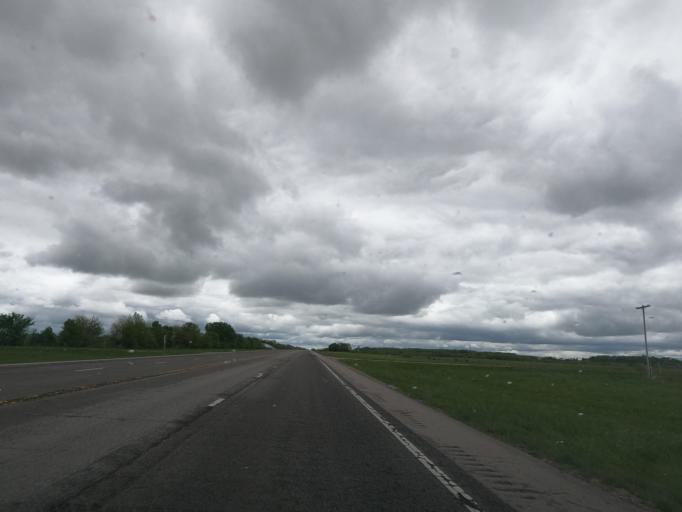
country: US
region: Kansas
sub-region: Montgomery County
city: Cherryvale
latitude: 37.3468
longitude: -95.5018
